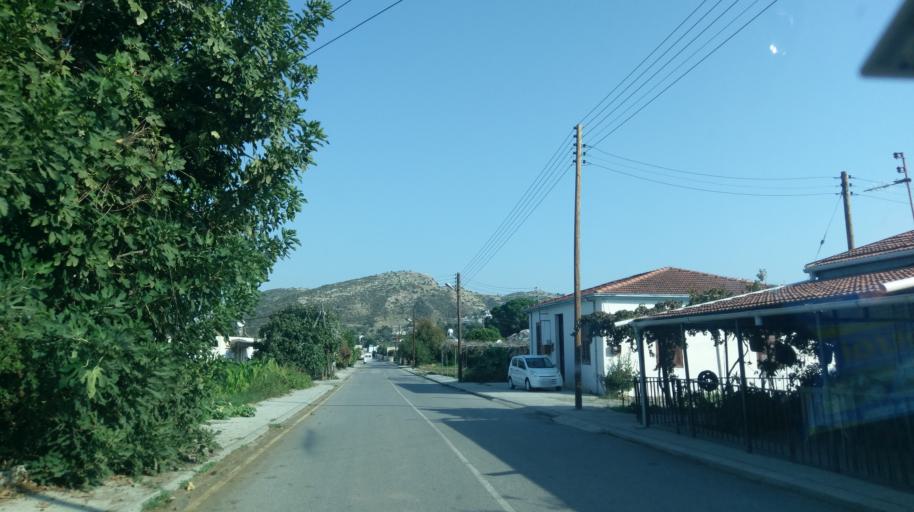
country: CY
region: Lefkosia
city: Kato Pyrgos
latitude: 35.1674
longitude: 32.7367
